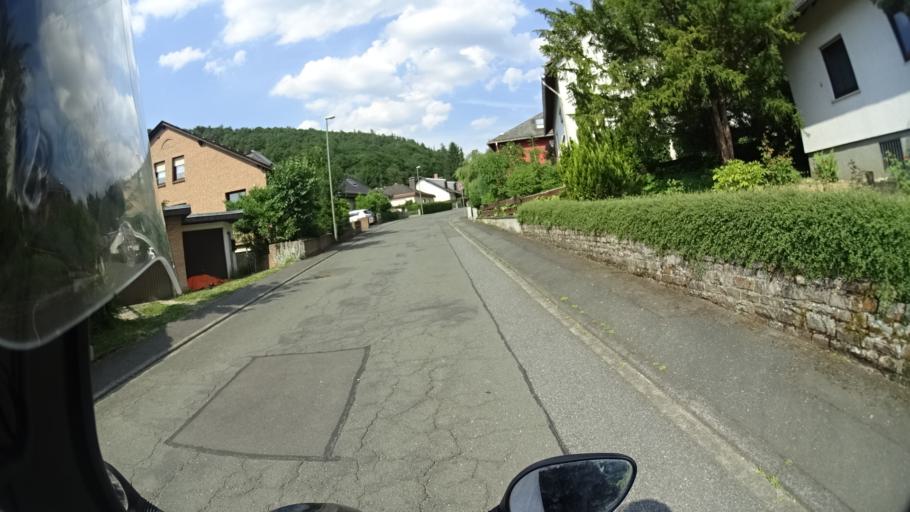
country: DE
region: Hesse
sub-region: Regierungsbezirk Darmstadt
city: Schlangenbad
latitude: 50.1093
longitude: 8.1013
